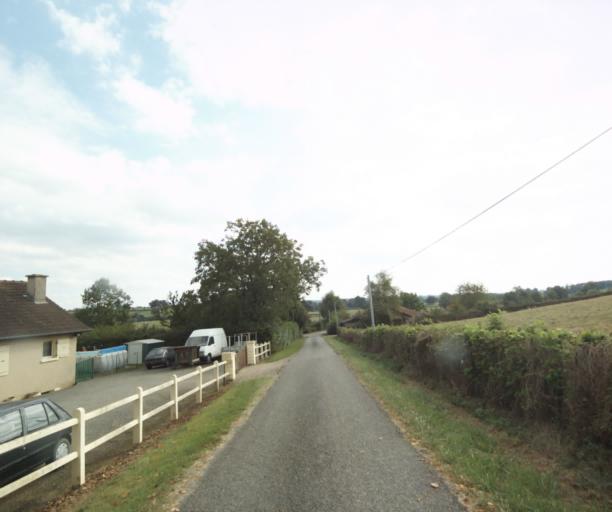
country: FR
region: Bourgogne
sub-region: Departement de Saone-et-Loire
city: Palinges
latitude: 46.5135
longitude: 4.1840
